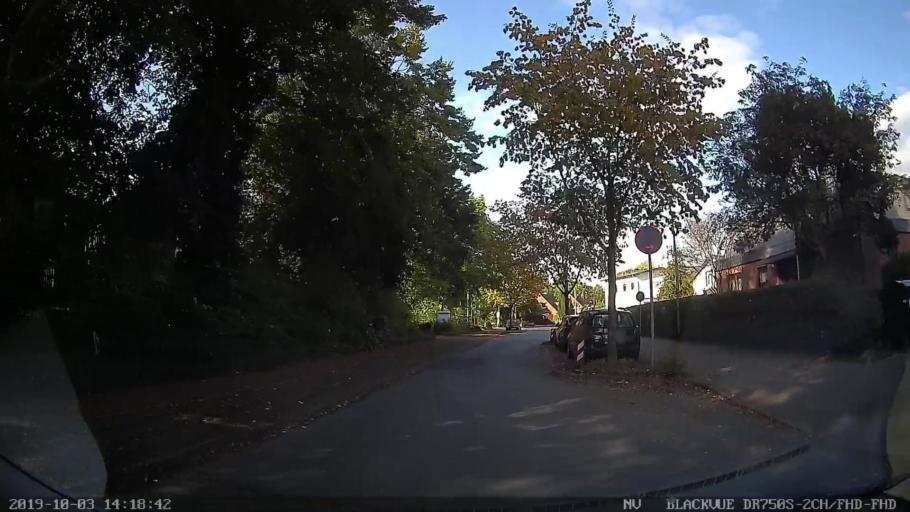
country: DE
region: Schleswig-Holstein
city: Pinneberg
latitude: 53.6661
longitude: 9.7963
